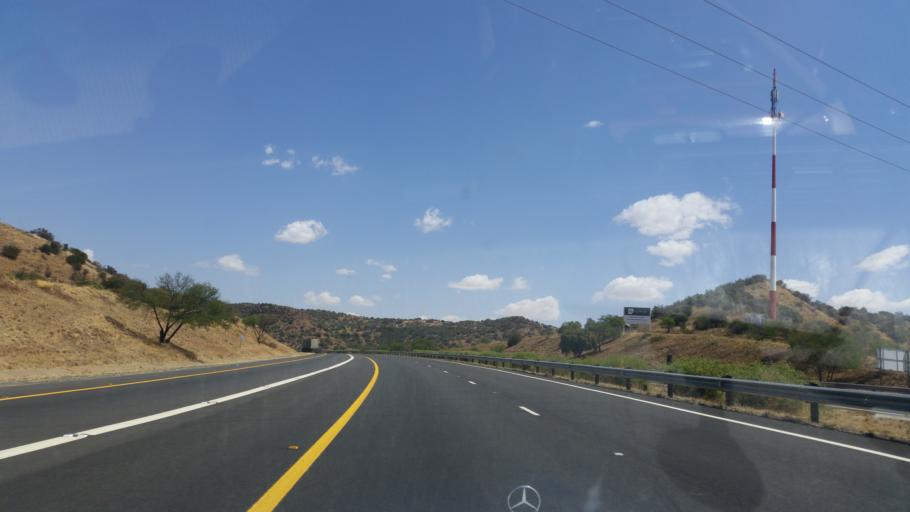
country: ZA
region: Orange Free State
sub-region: Mangaung Metropolitan Municipality
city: Bloemfontein
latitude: -28.9789
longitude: 26.2851
